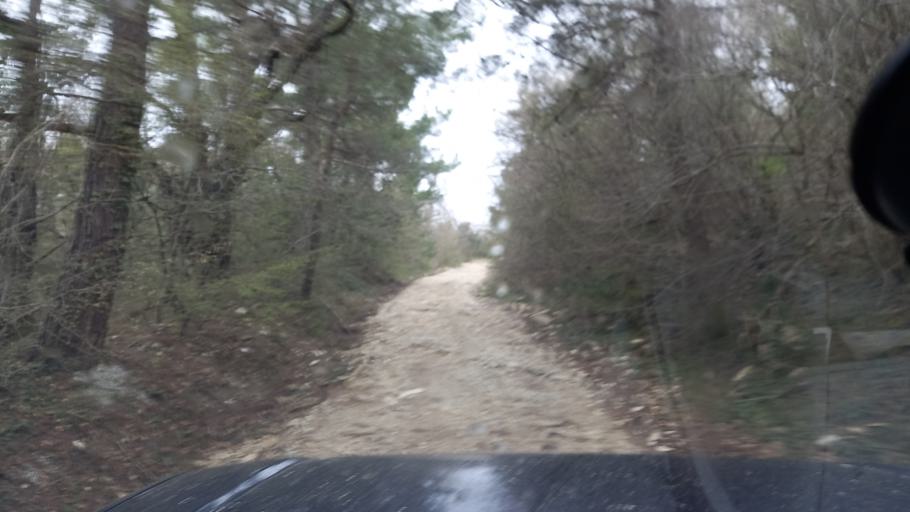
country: RU
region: Krasnodarskiy
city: Arkhipo-Osipovka
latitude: 44.3701
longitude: 38.4550
